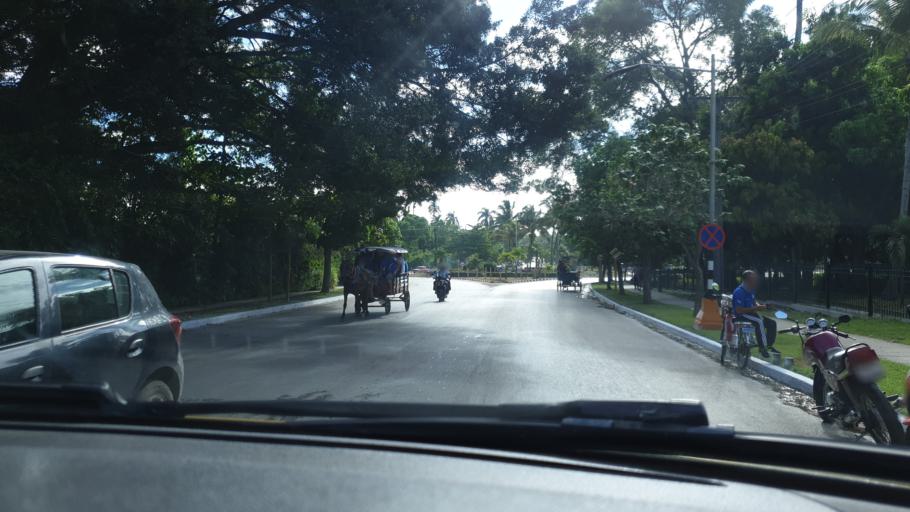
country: CU
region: Villa Clara
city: Santa Clara
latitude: 22.4152
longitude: -79.9473
